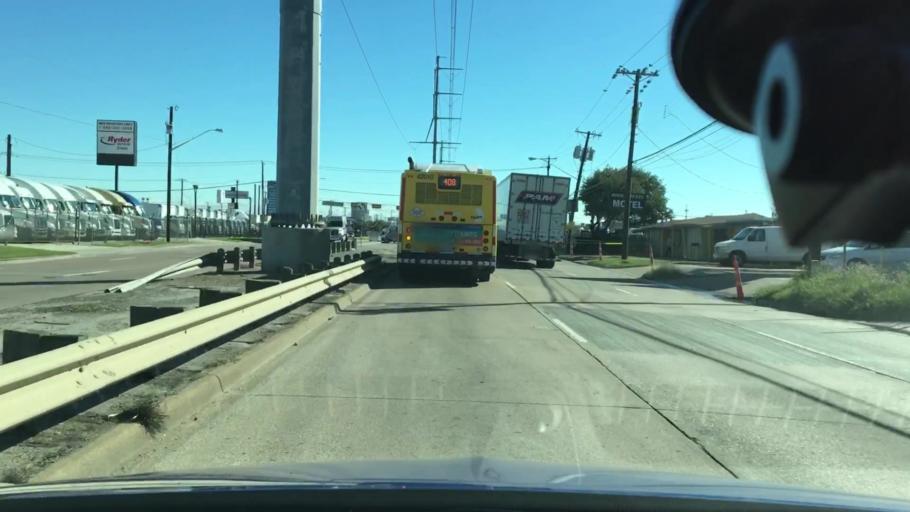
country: US
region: Texas
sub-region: Dallas County
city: Cockrell Hill
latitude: 32.8080
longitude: -96.8752
